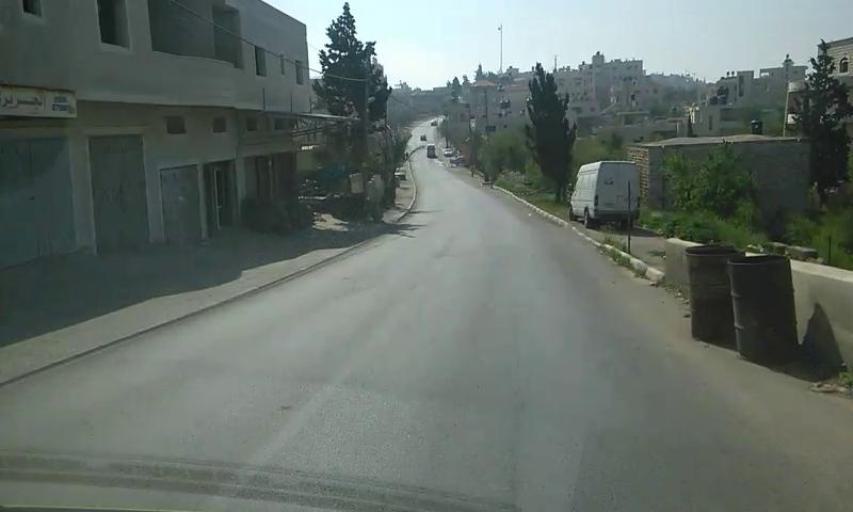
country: PS
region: West Bank
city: Dayr Jarir
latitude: 31.9613
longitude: 35.2958
